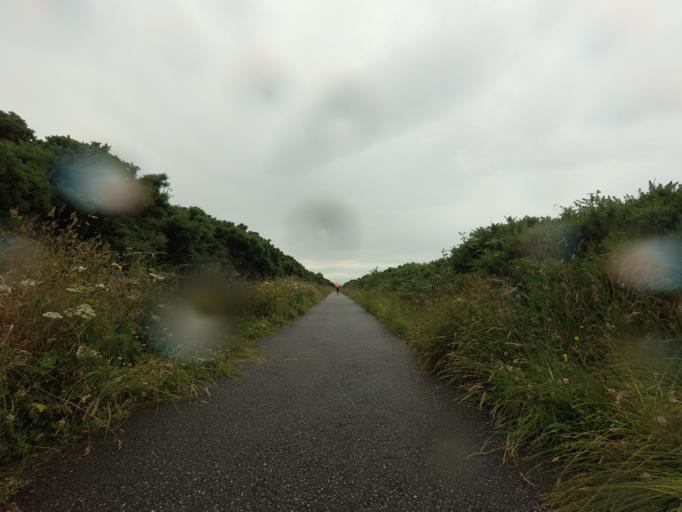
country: GB
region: Scotland
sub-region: Moray
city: Findochty
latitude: 57.6929
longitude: -2.9086
